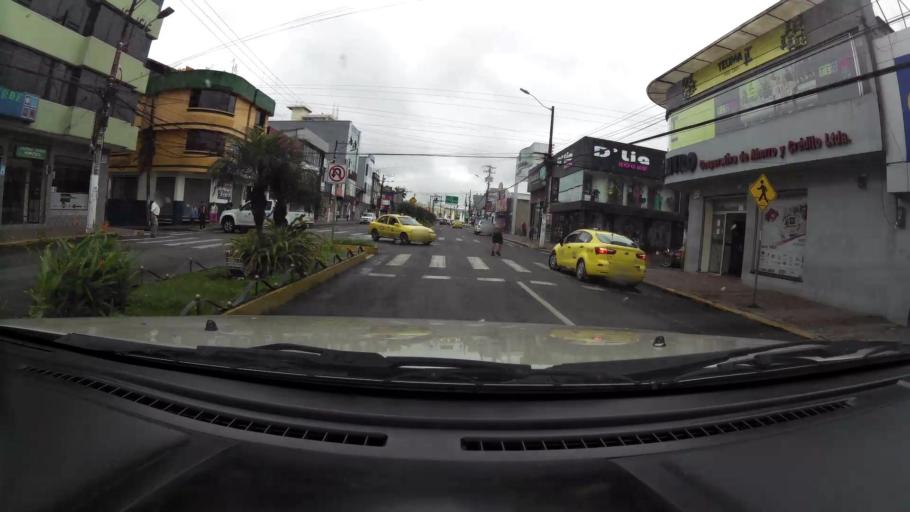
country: EC
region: Santo Domingo de los Tsachilas
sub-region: Canton Santo Domingo de los Colorados
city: Santo Domingo de los Colorados
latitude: -0.2512
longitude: -79.1639
